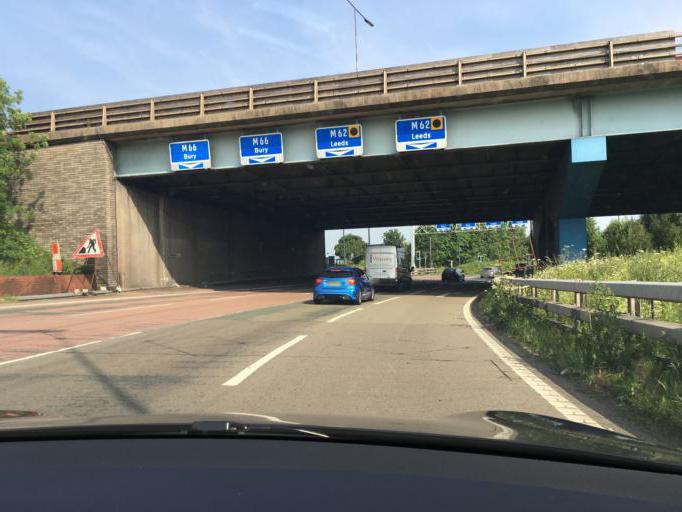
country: GB
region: England
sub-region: Borough of Bury
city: Prestwich
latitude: 53.5491
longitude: -2.2612
